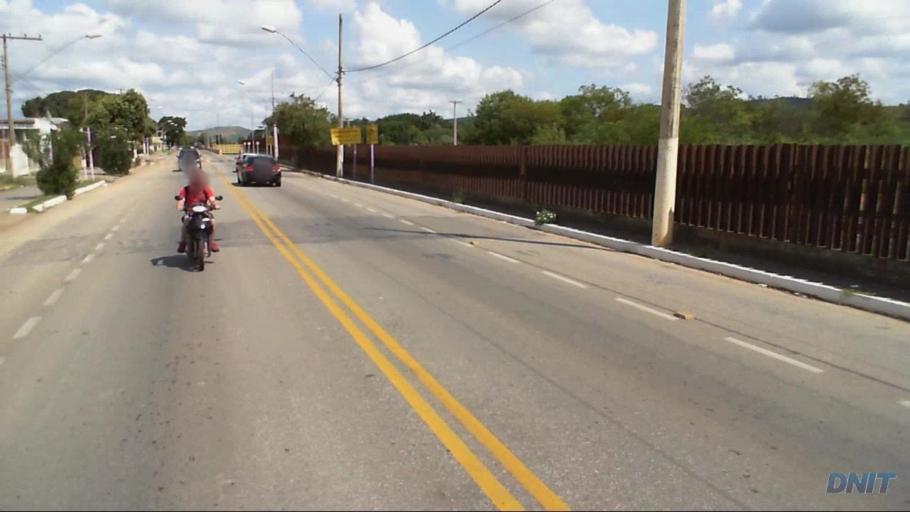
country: BR
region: Minas Gerais
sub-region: Governador Valadares
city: Governador Valadares
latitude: -18.9024
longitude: -41.9873
